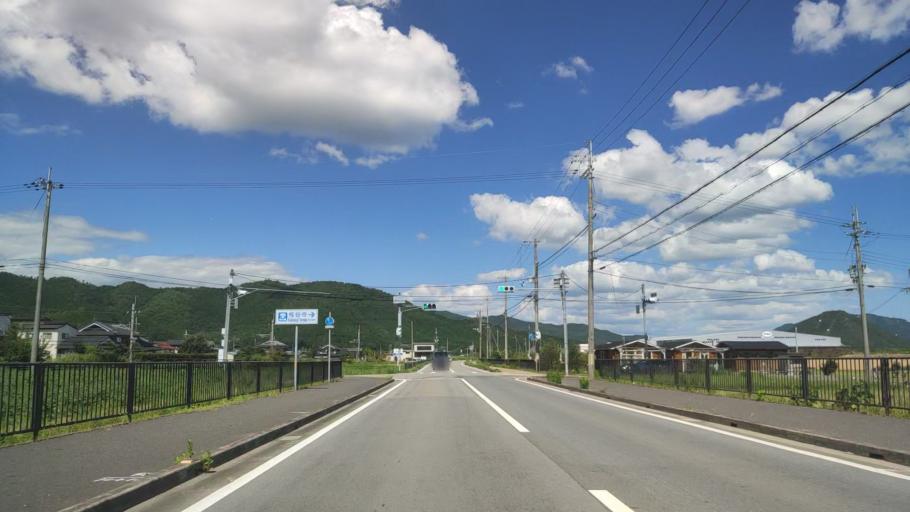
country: JP
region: Kyoto
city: Fukuchiyama
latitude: 35.1691
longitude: 135.1176
